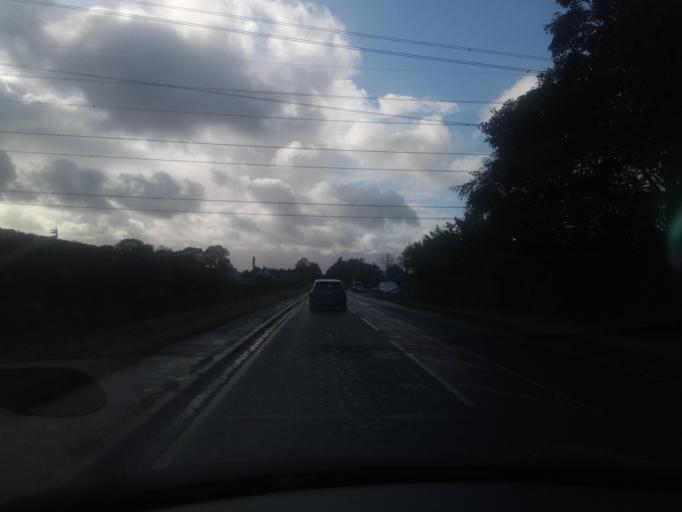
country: GB
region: England
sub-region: Cumbria
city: Carlisle
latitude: 54.9415
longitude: -2.9440
